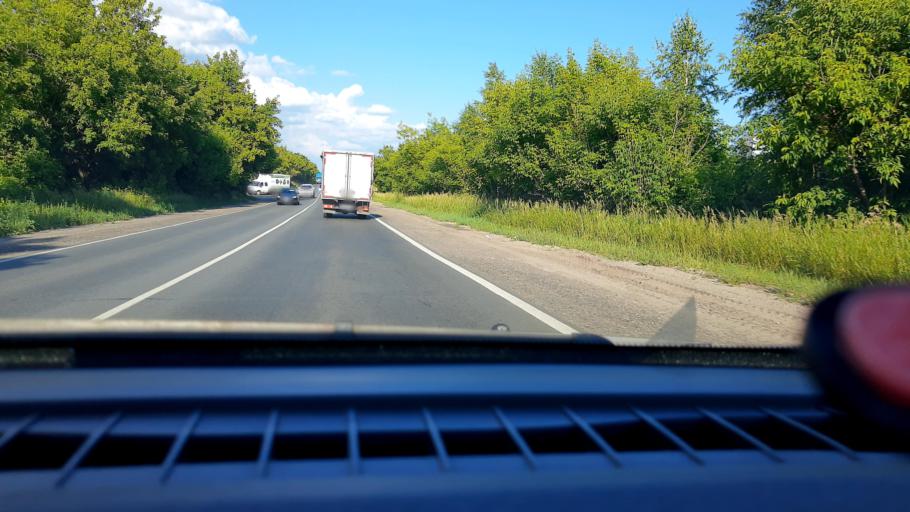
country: RU
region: Nizjnij Novgorod
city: Babino
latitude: 56.2572
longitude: 43.6190
